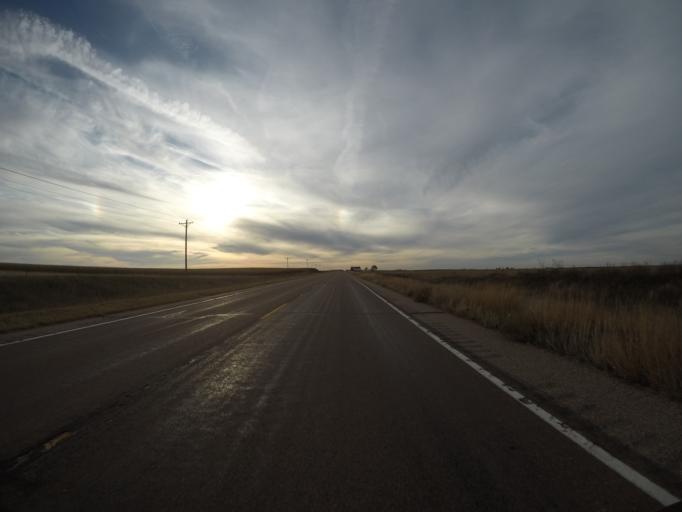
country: US
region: Colorado
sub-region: Yuma County
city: Yuma
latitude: 39.6560
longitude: -102.6418
